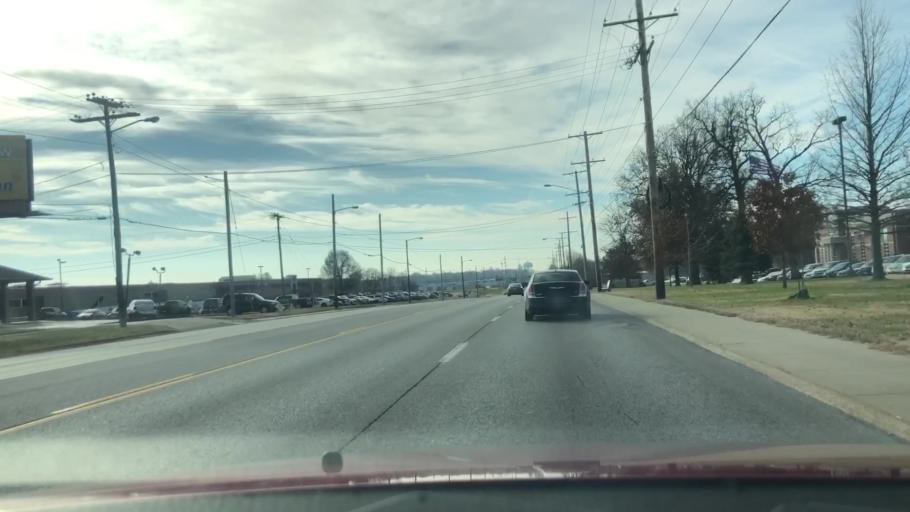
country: US
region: Missouri
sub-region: Greene County
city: Springfield
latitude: 37.2227
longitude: -93.2616
